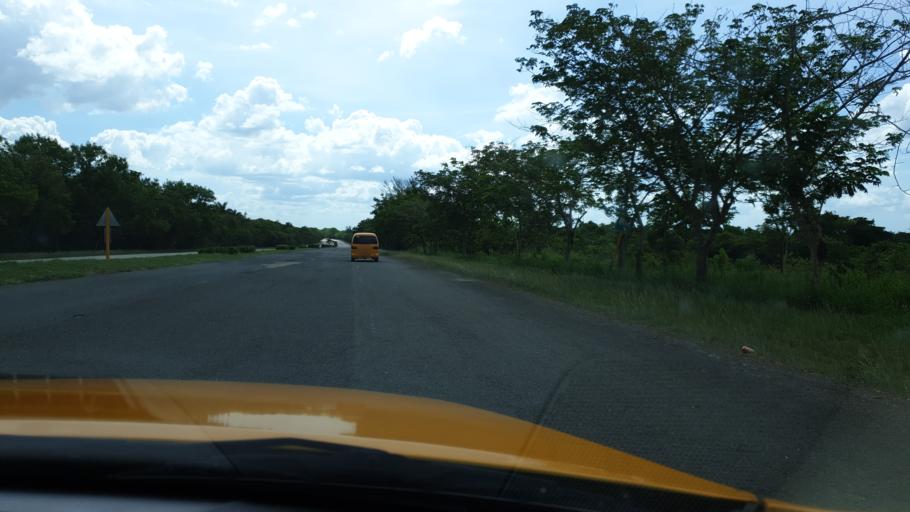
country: CU
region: Cienfuegos
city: Cruces
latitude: 22.4538
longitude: -80.2960
